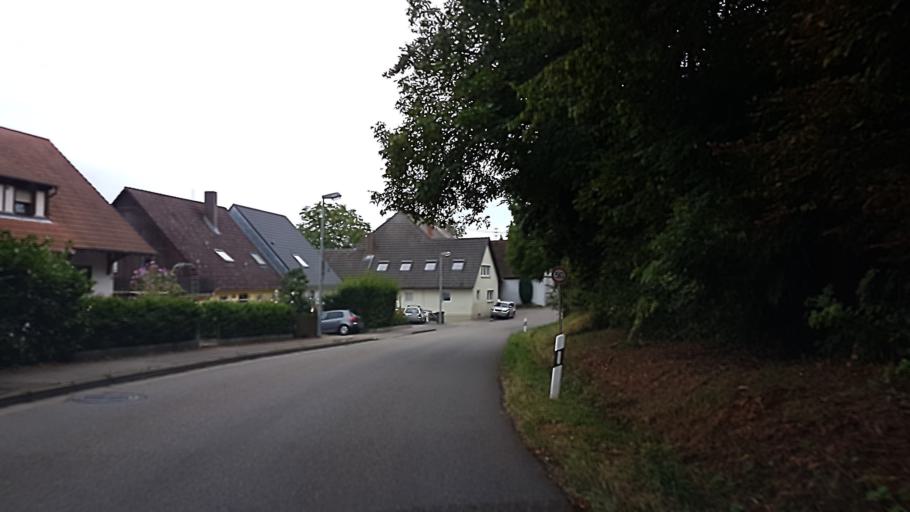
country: DE
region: Baden-Wuerttemberg
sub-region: Freiburg Region
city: Gottenheim
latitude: 48.0109
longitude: 7.7245
